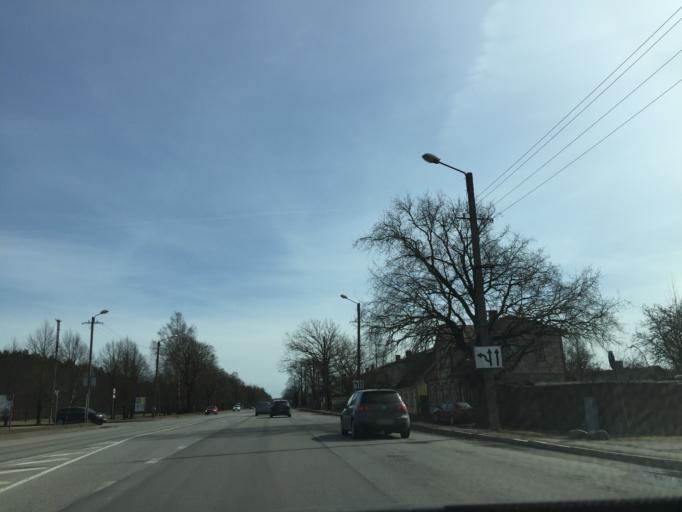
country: EE
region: Paernumaa
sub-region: Paernu linn
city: Parnu
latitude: 58.3685
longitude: 24.5506
